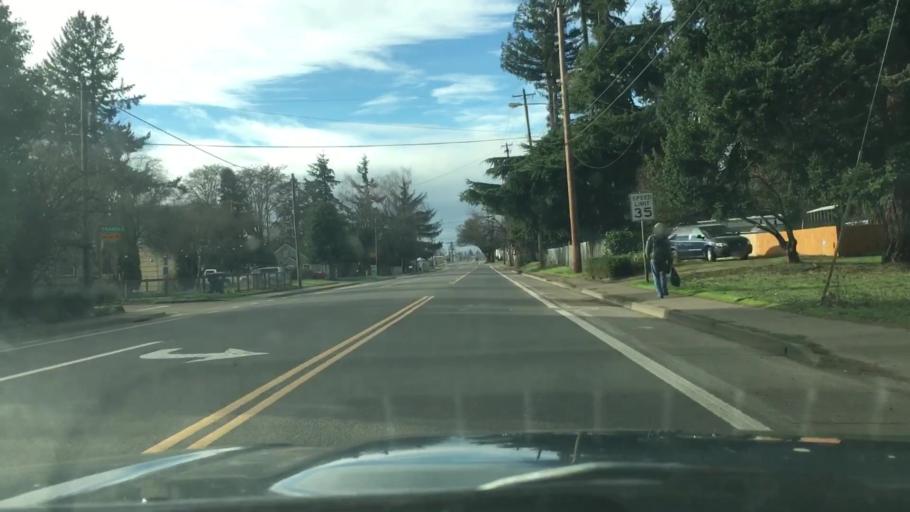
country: US
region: Oregon
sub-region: Lane County
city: Eugene
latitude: 44.0637
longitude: -123.1298
